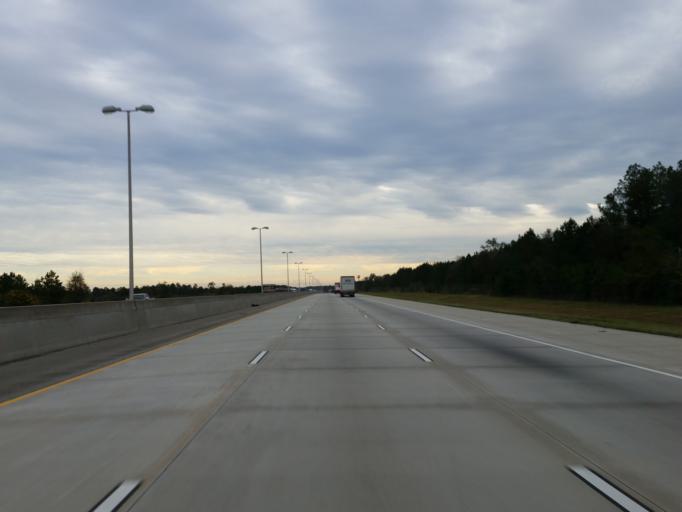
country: US
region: Georgia
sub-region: Cook County
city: Adel
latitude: 31.0844
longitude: -83.4131
